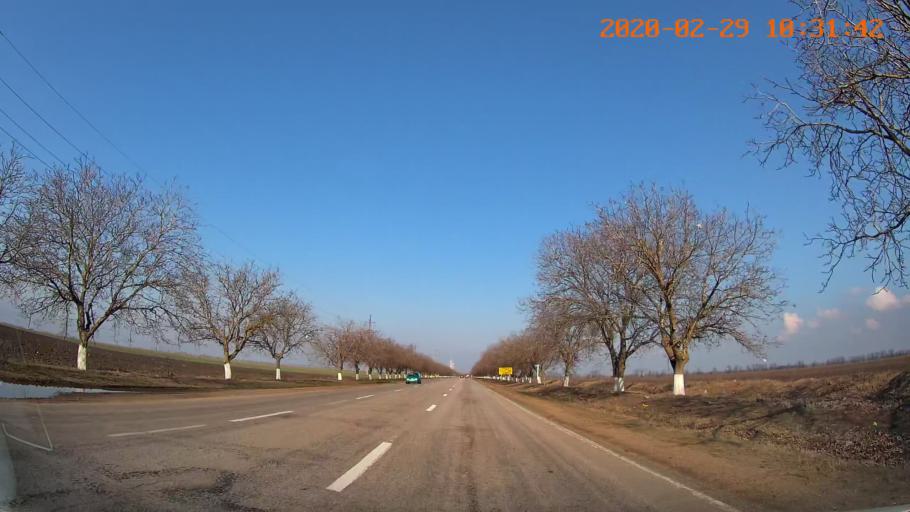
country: UA
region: Odessa
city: Velykoploske
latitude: 46.9517
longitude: 29.5611
